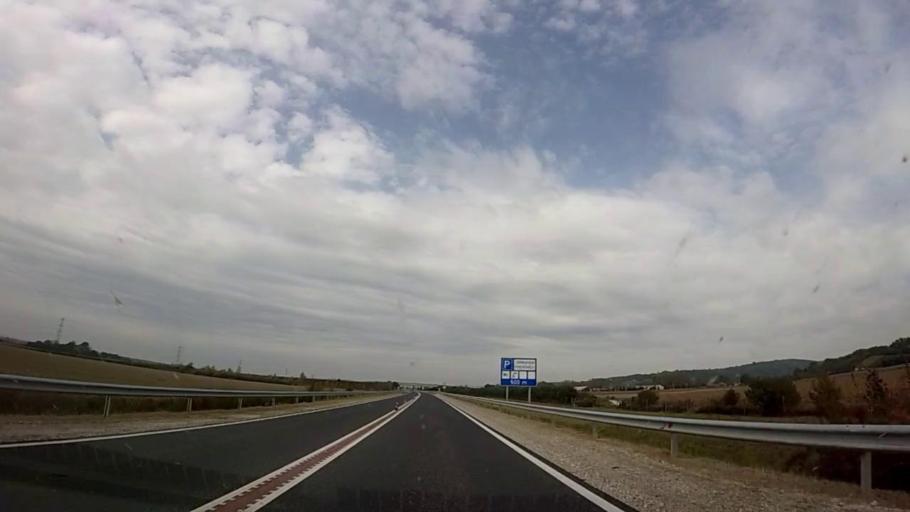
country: HR
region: Medimurska
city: Domasinec
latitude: 46.4985
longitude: 16.6219
